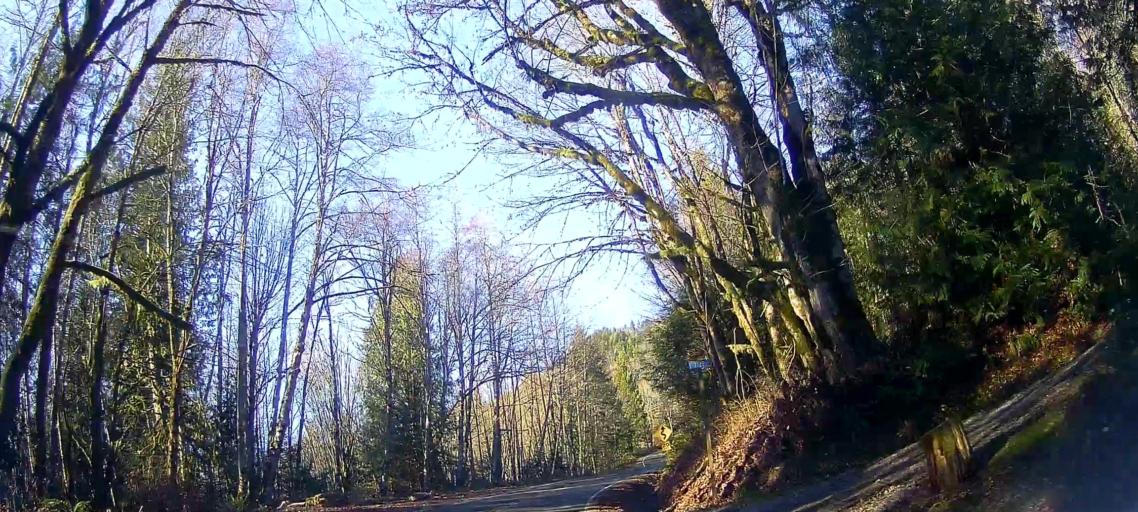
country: US
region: Washington
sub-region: Snohomish County
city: Darrington
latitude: 48.5416
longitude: -121.7646
